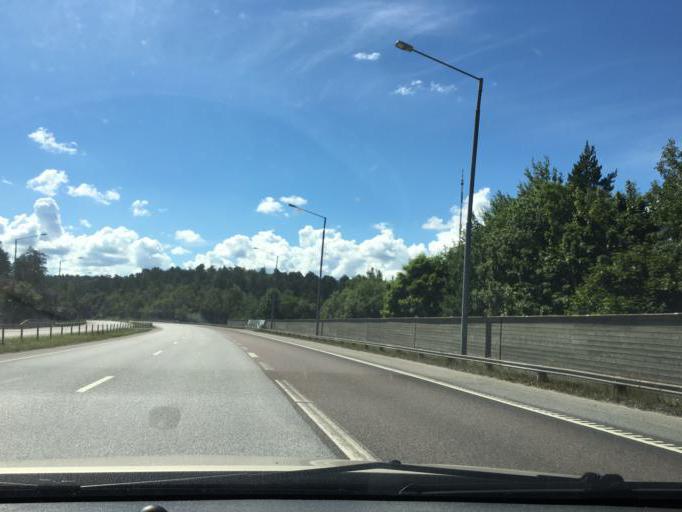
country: SE
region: Stockholm
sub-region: Nacka Kommun
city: Nacka
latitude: 59.3066
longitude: 18.1811
